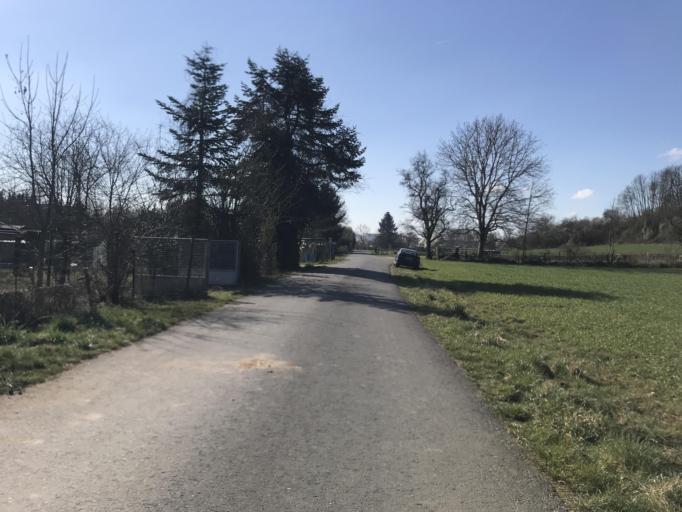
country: DE
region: Hesse
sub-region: Regierungsbezirk Darmstadt
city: Florsheim
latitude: 50.0081
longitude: 8.4066
